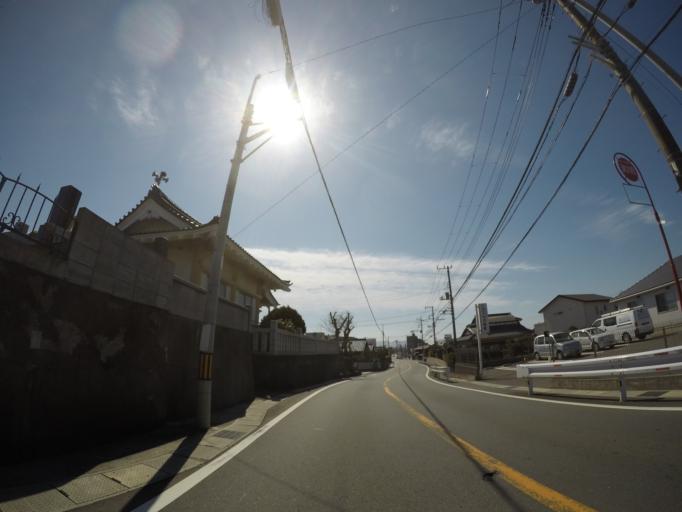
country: JP
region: Shizuoka
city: Numazu
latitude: 35.1244
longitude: 138.8353
